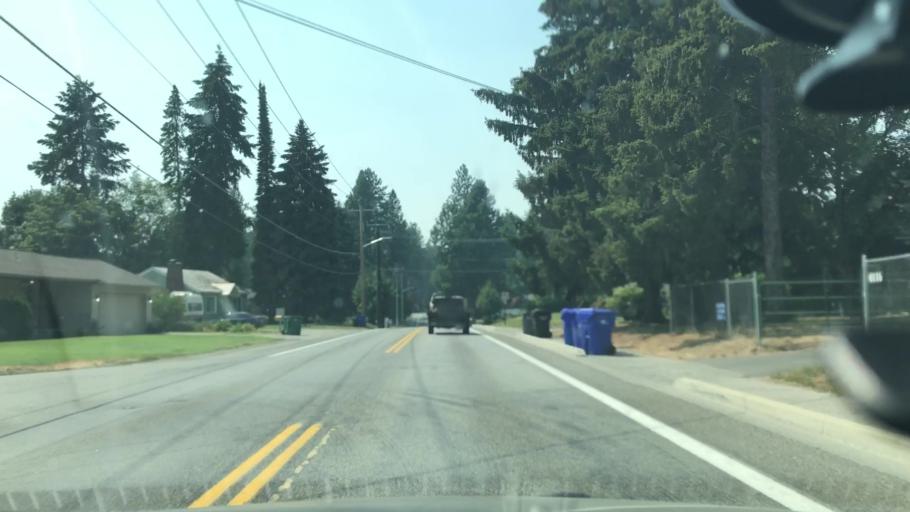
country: US
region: Washington
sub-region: Spokane County
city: Millwood
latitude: 47.6973
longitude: -117.2952
